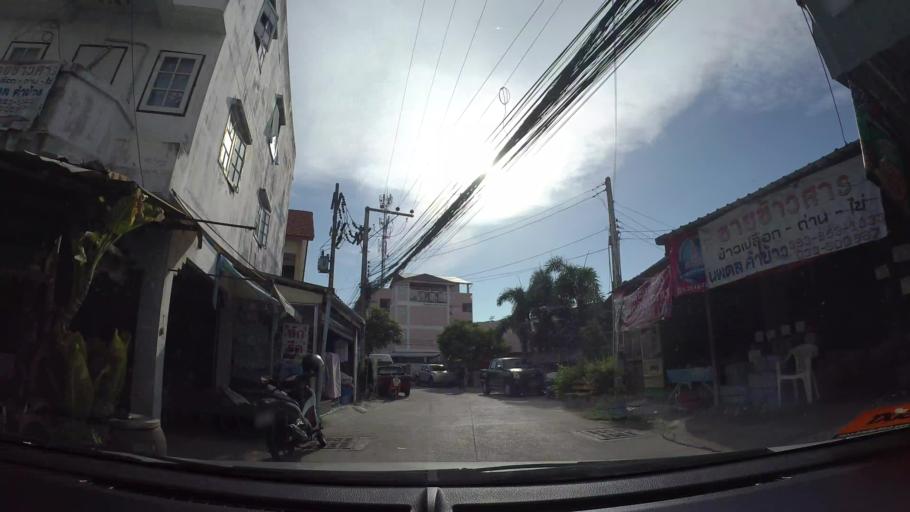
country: TH
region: Chon Buri
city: Phatthaya
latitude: 12.9136
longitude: 100.8800
